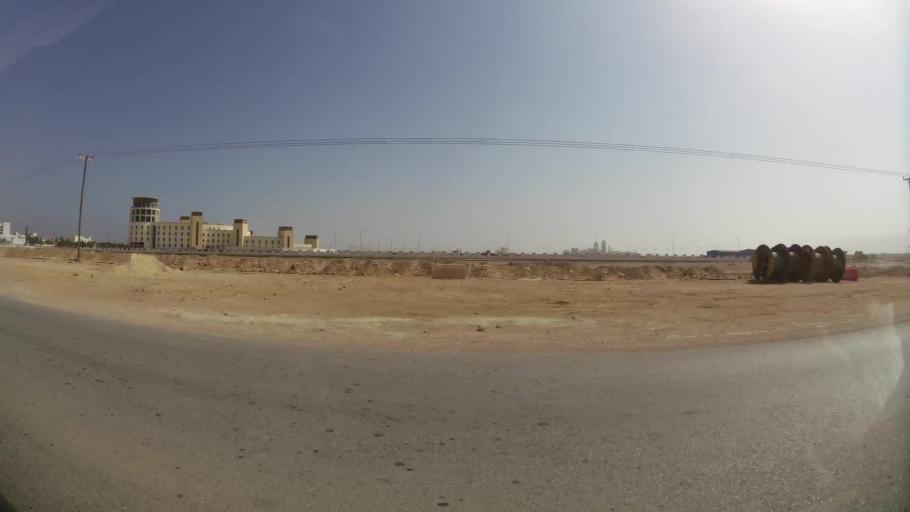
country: OM
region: Zufar
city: Salalah
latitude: 16.9879
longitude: 54.0149
